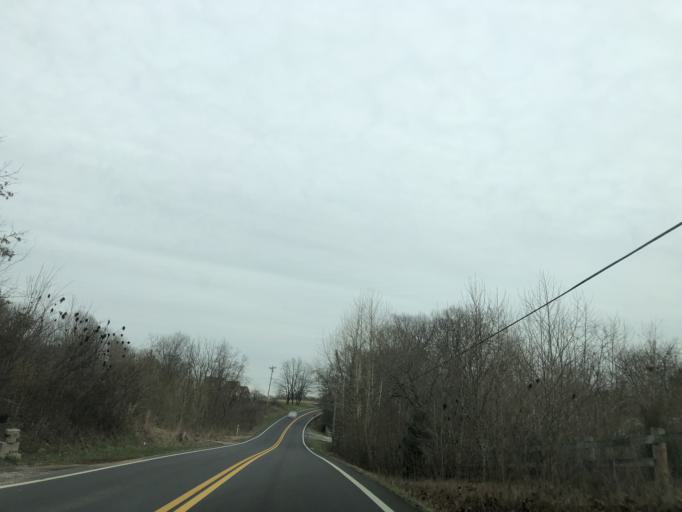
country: US
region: Tennessee
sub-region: Sumner County
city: White House
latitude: 36.4765
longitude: -86.7273
